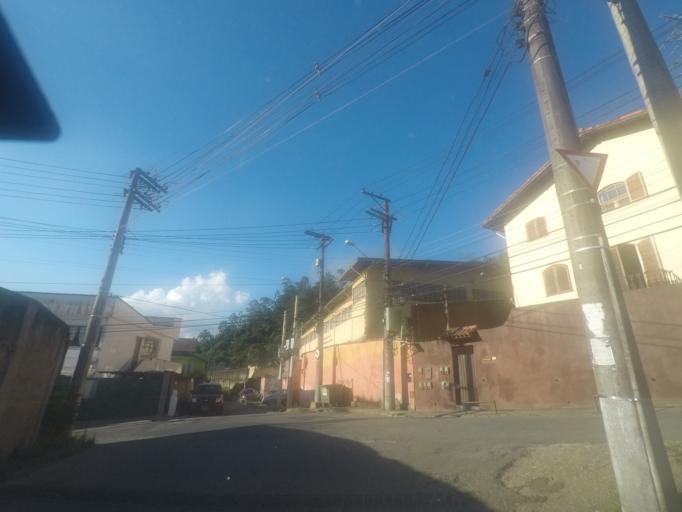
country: BR
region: Rio de Janeiro
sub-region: Petropolis
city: Petropolis
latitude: -22.4864
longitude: -43.1503
